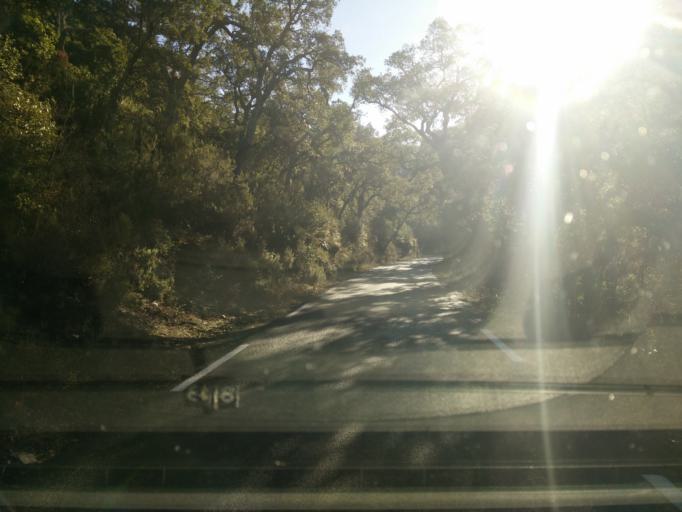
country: FR
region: Provence-Alpes-Cote d'Azur
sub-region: Departement du Var
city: Collobrieres
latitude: 43.2386
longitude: 6.3351
